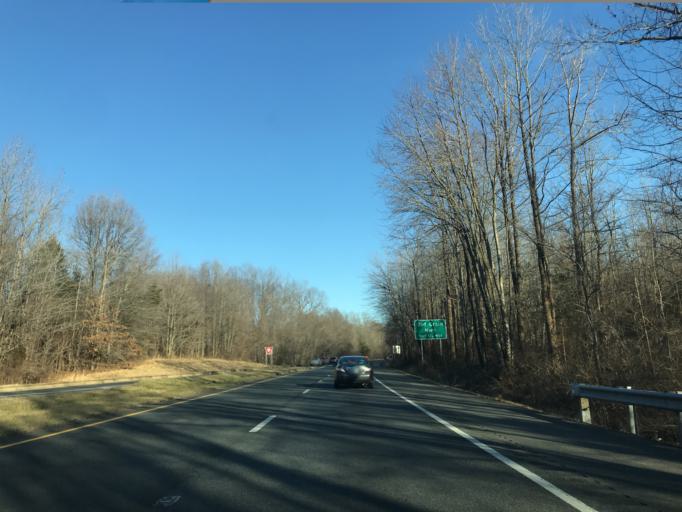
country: US
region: Maryland
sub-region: Prince George's County
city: Upper Marlboro
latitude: 38.8118
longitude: -76.7749
